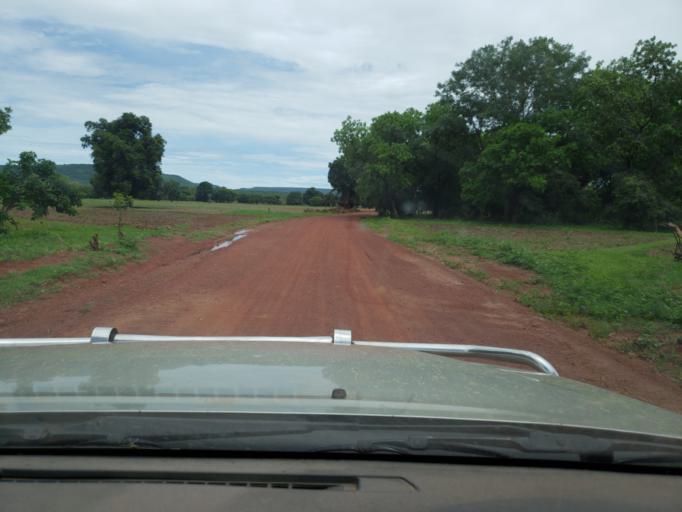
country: ML
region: Sikasso
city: Sikasso
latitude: 11.6728
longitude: -6.3380
